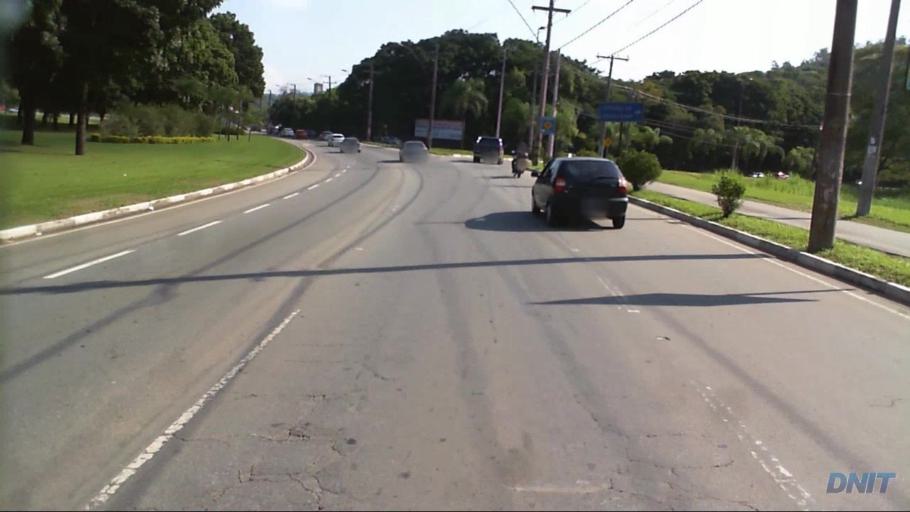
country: BR
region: Minas Gerais
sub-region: Ipatinga
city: Ipatinga
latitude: -19.4840
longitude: -42.5543
